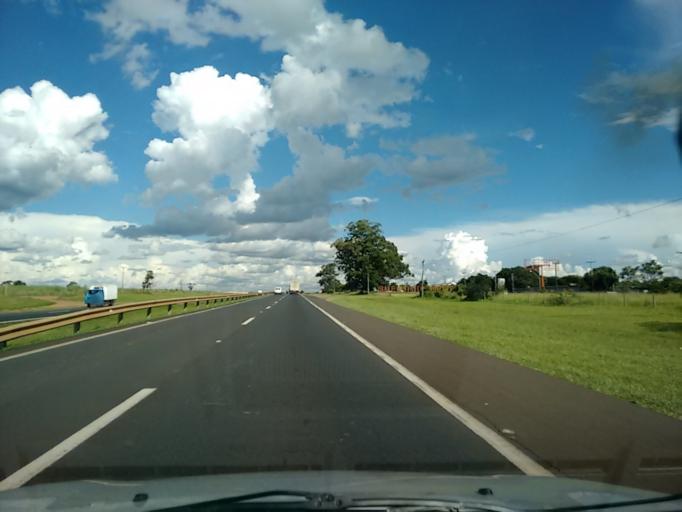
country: BR
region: Sao Paulo
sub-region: Ibate
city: Ibate
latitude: -21.9268
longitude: -48.0259
